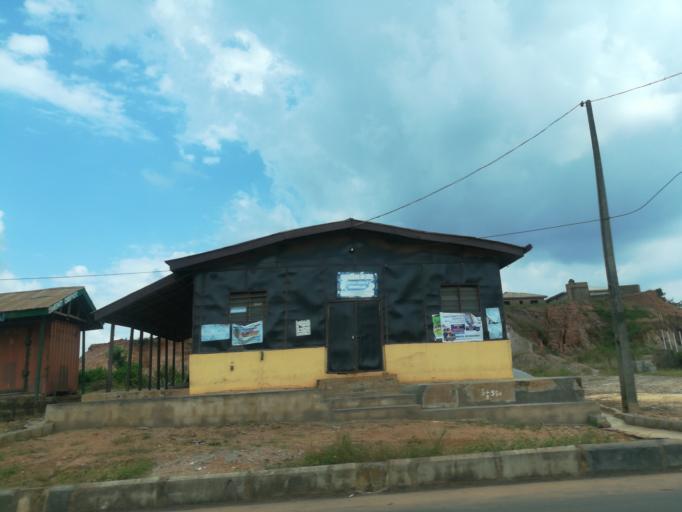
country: NG
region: Oyo
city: Ibadan
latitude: 7.4305
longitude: 3.8364
